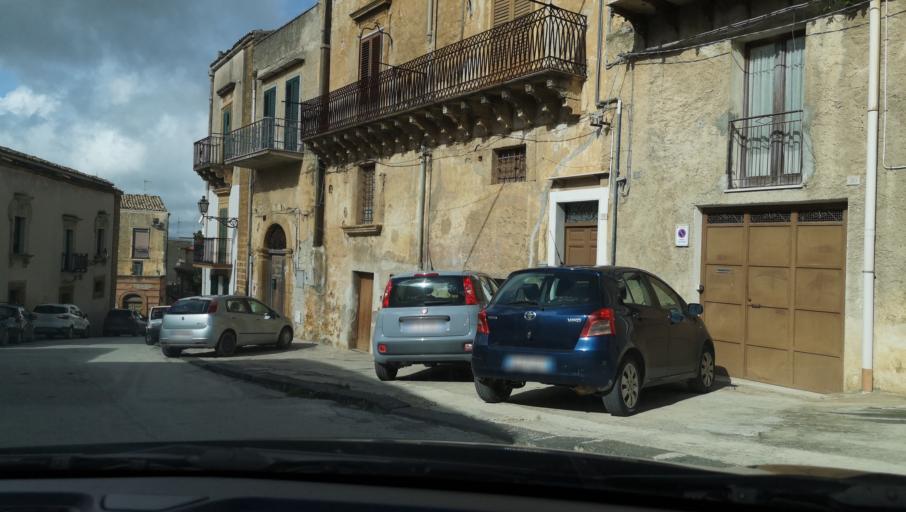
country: IT
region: Sicily
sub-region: Agrigento
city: Sambuca di Sicilia
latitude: 37.6491
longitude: 13.1132
